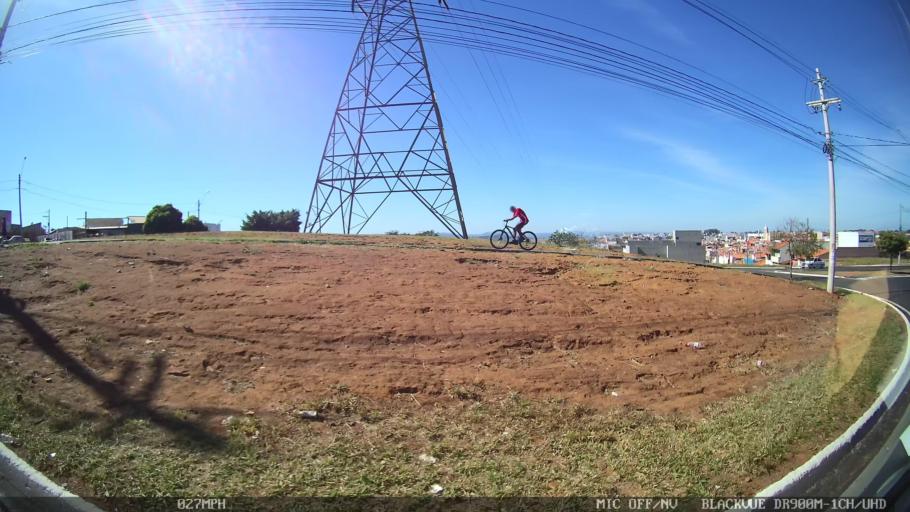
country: BR
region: Sao Paulo
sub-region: Franca
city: Franca
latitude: -20.5444
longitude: -47.3593
